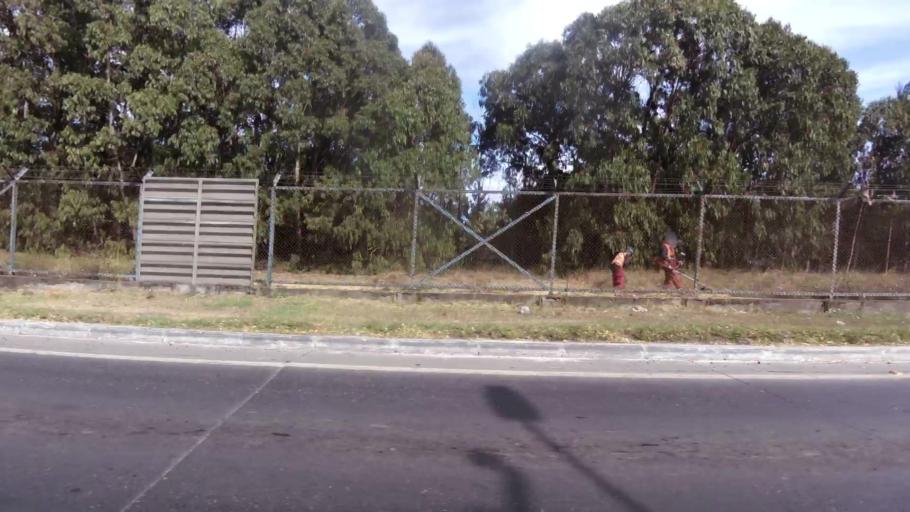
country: CL
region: Biobio
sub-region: Provincia de Concepcion
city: Talcahuano
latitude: -36.7364
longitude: -73.1203
